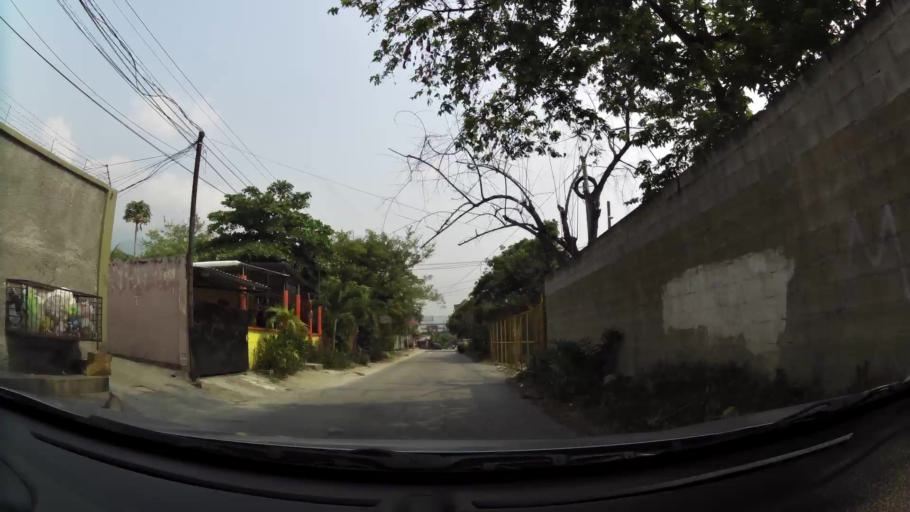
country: HN
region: Cortes
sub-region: San Pedro Sula
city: Pena Blanca
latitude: 15.5264
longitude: -88.0312
